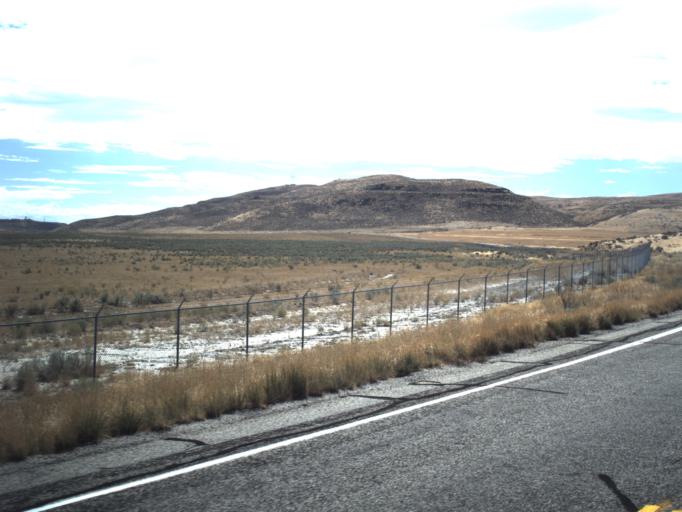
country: US
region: Utah
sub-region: Box Elder County
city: Tremonton
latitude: 41.7215
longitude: -112.4497
